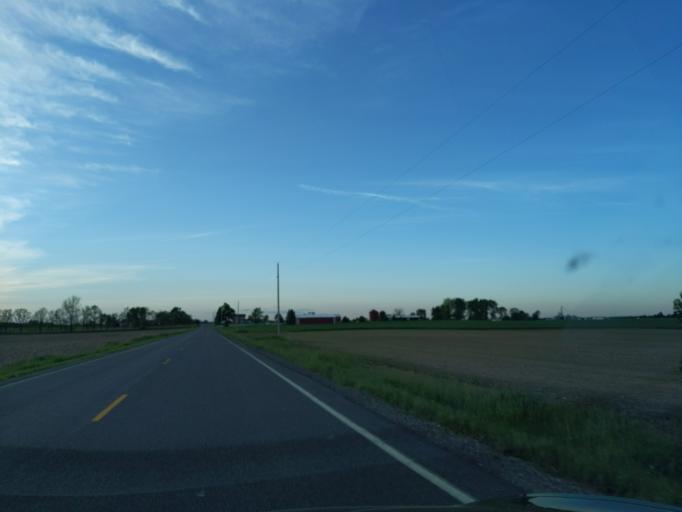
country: US
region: Michigan
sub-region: Ingham County
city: Williamston
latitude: 42.5903
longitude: -84.2987
